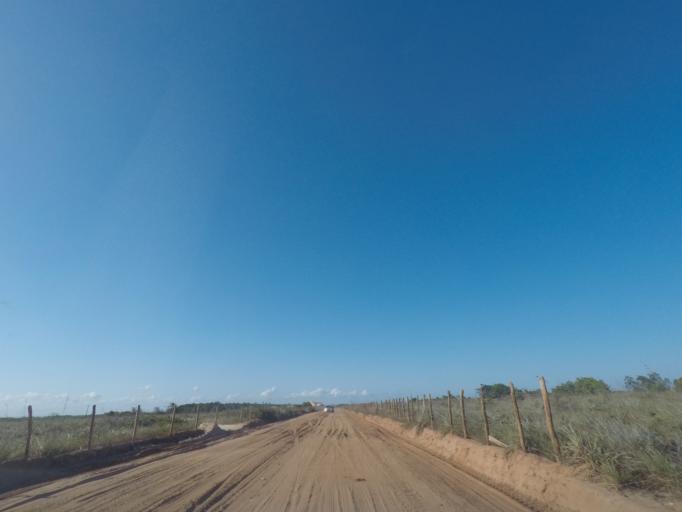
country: BR
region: Bahia
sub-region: Camamu
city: Camamu
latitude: -13.9407
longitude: -38.9457
